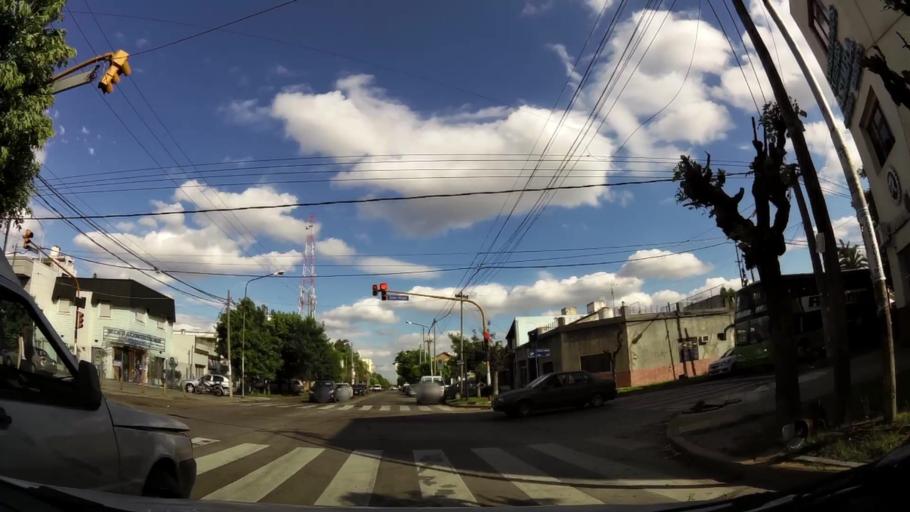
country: AR
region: Buenos Aires
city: San Justo
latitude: -34.6802
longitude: -58.5651
